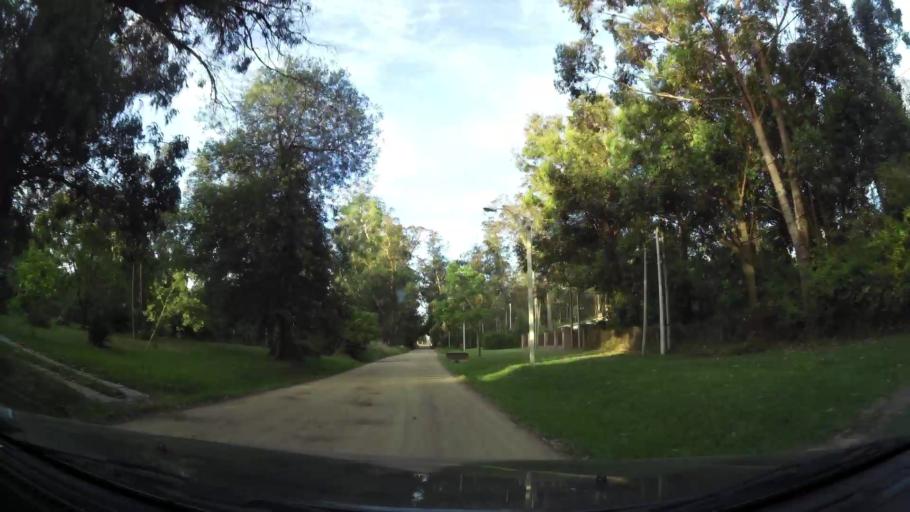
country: UY
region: Canelones
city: Atlantida
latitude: -34.7707
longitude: -55.8043
